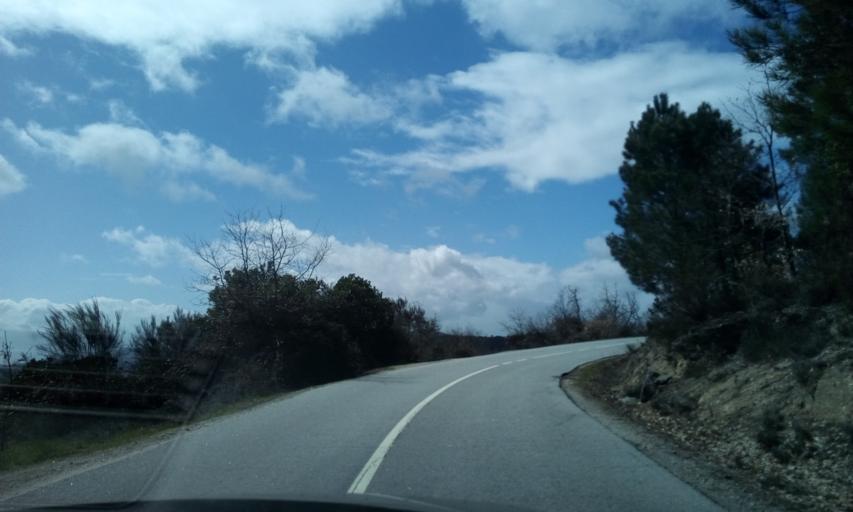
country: PT
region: Guarda
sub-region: Fornos de Algodres
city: Fornos de Algodres
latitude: 40.6335
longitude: -7.5467
